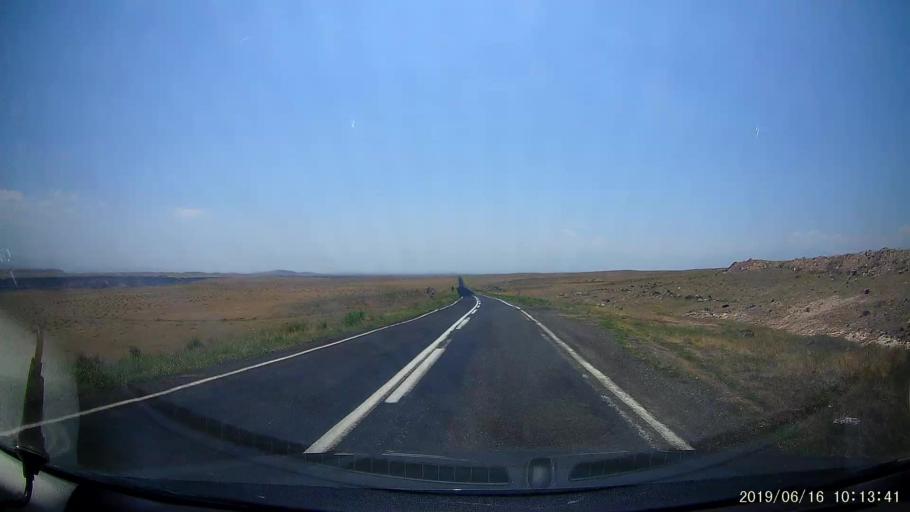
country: TR
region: Igdir
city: Tuzluca
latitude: 40.1914
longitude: 43.6473
